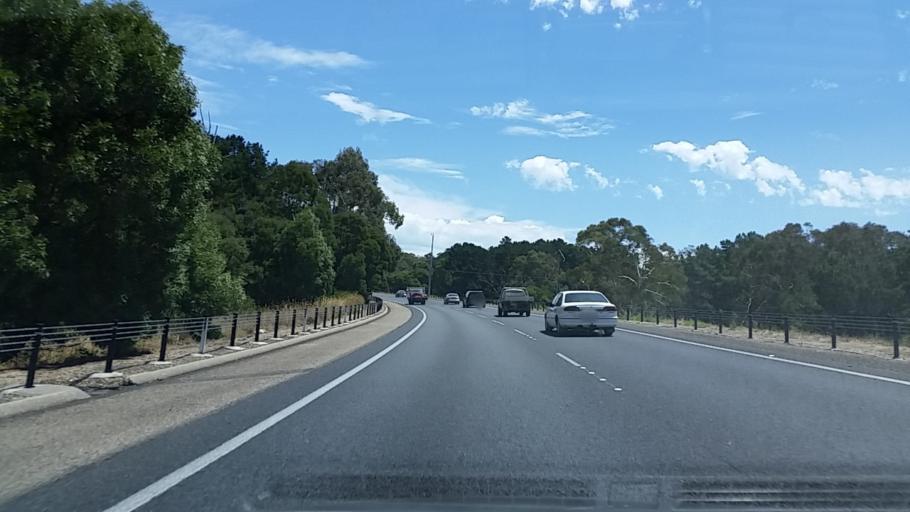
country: AU
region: South Australia
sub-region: Adelaide Hills
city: Bridgewater
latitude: -34.9947
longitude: 138.7363
